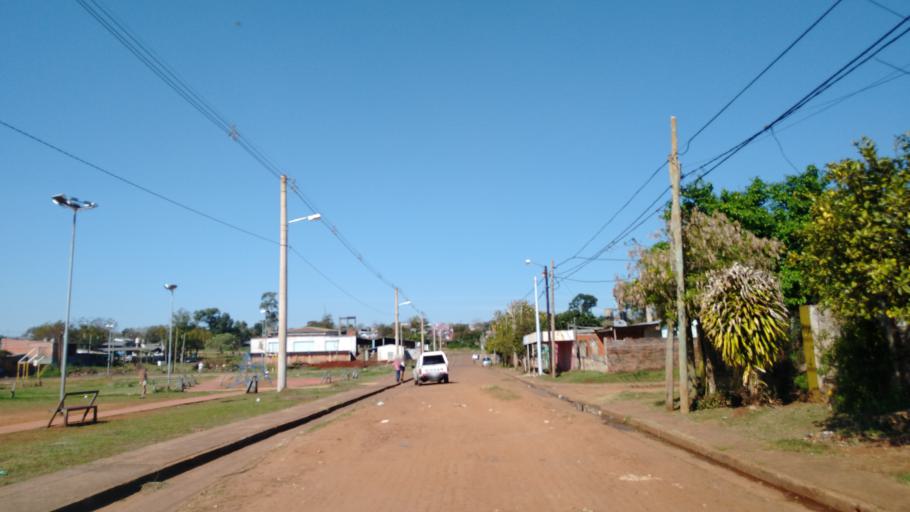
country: AR
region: Misiones
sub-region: Departamento de Capital
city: Posadas
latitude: -27.4115
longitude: -55.9577
